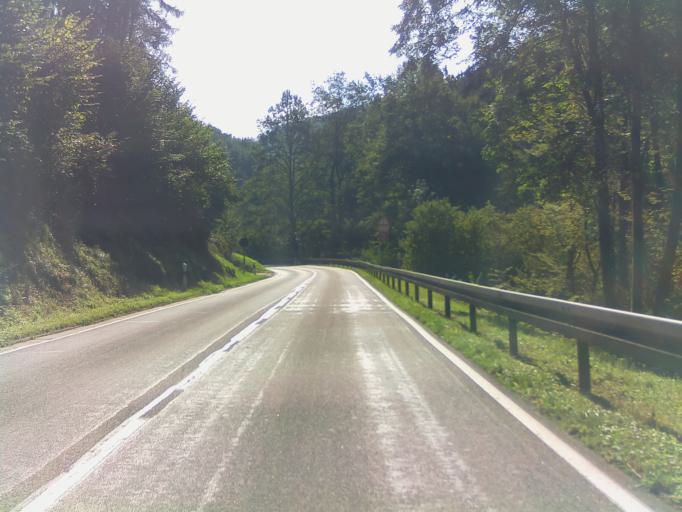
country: DE
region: Hesse
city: Hirschhorn
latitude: 49.4588
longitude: 8.8712
